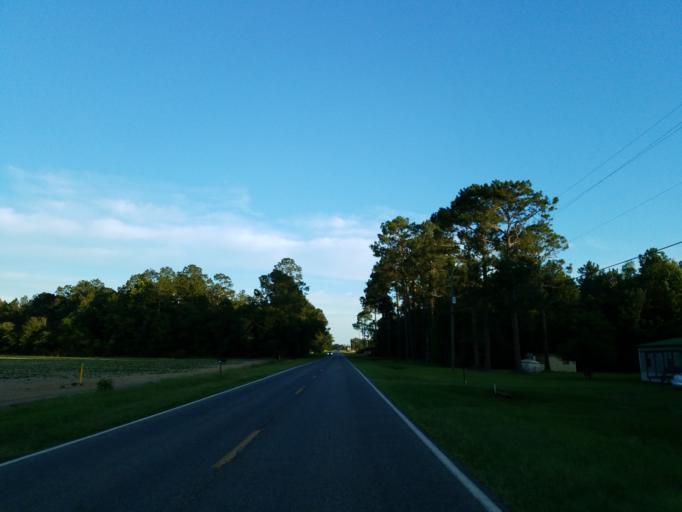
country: US
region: Georgia
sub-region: Cook County
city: Sparks
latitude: 31.2004
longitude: -83.4490
